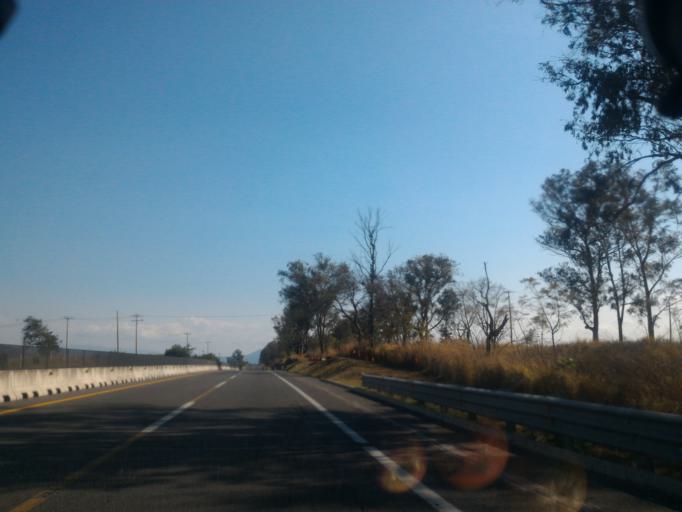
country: MX
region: Jalisco
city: Zapotiltic
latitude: 19.6116
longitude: -103.4590
